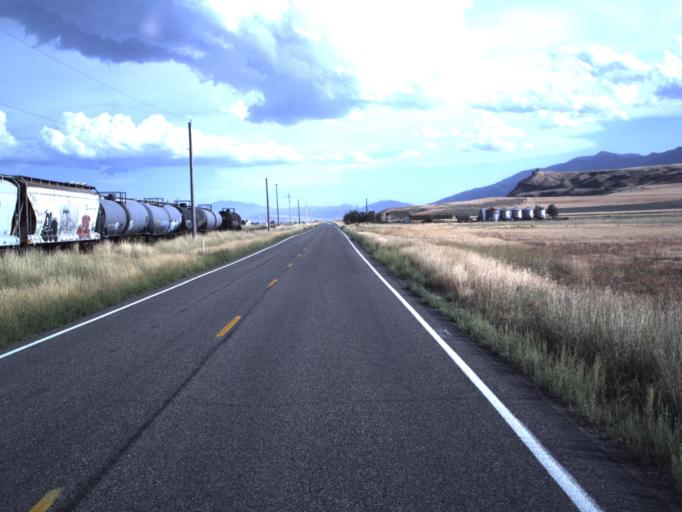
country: US
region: Utah
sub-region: Cache County
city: Benson
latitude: 41.8273
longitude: -112.0005
